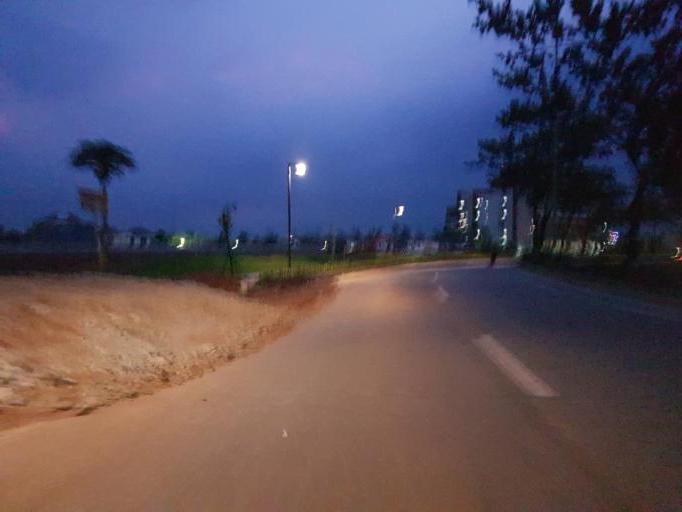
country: ID
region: West Java
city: Serpong
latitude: -6.3166
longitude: 106.6522
